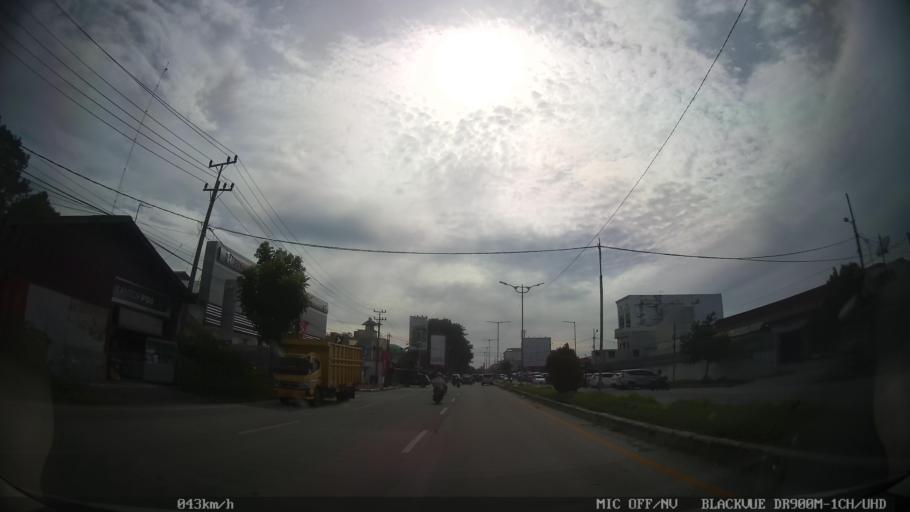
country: ID
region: North Sumatra
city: Medan
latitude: 3.6293
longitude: 98.6920
